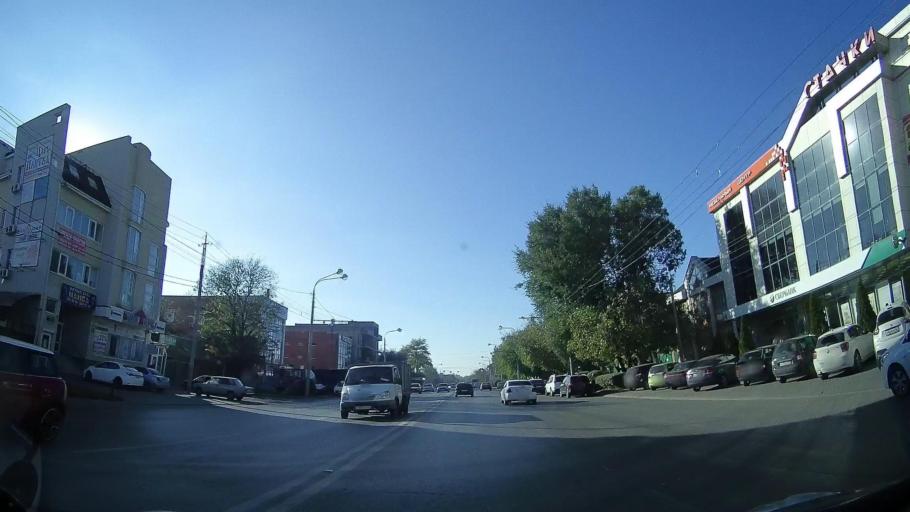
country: RU
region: Rostov
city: Rostov-na-Donu
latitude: 47.2113
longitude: 39.6659
